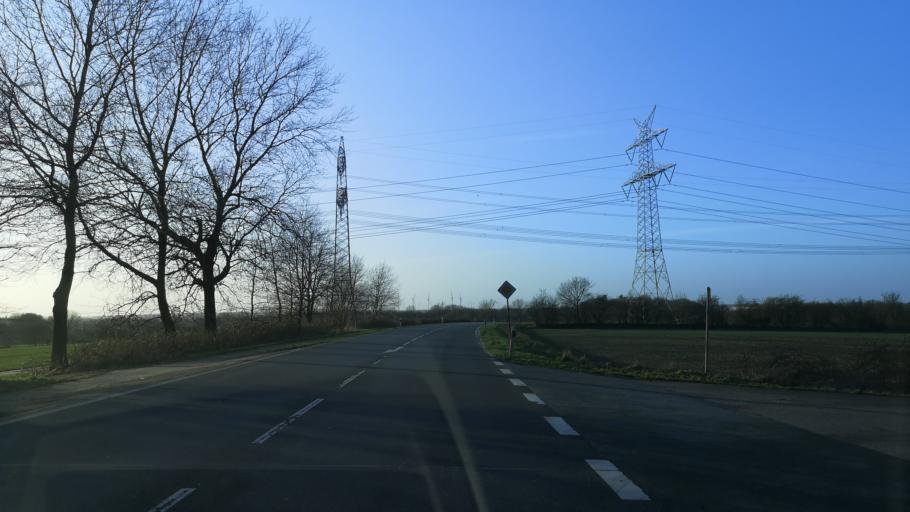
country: DE
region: Schleswig-Holstein
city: Tarp
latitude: 54.6640
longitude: 9.4226
